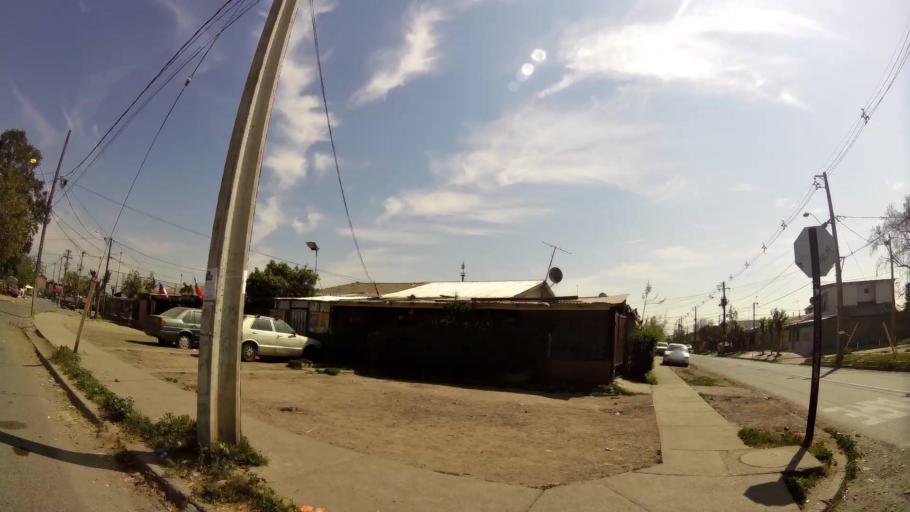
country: CL
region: Santiago Metropolitan
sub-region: Provincia de Santiago
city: La Pintana
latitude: -33.5622
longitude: -70.6447
